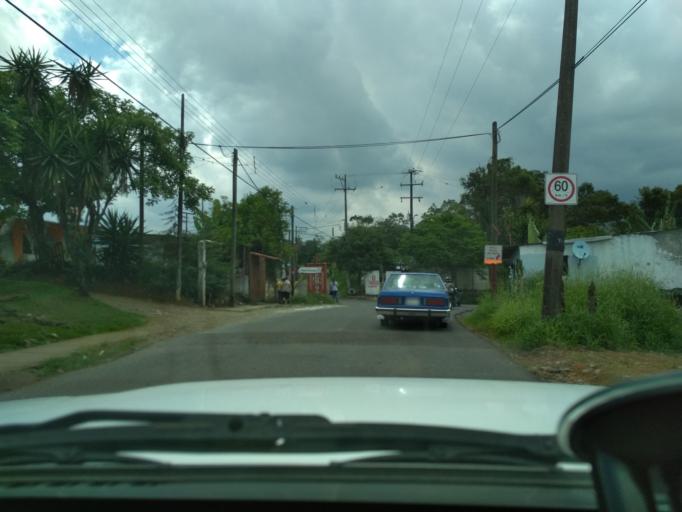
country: MX
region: Veracruz
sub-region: Cordoba
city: San Jose de Abajo [Unidad Habitacional]
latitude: 18.9226
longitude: -96.9650
